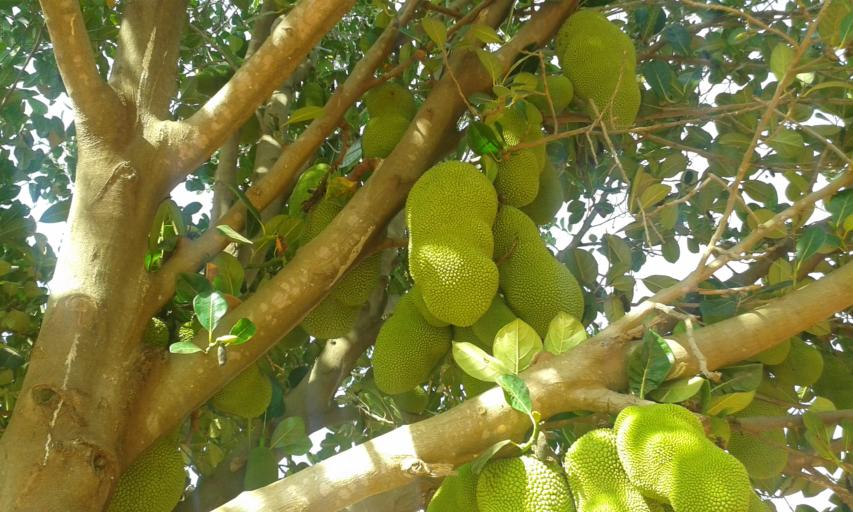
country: UG
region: Northern Region
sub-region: Gulu District
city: Gulu
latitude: 2.7891
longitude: 32.3167
